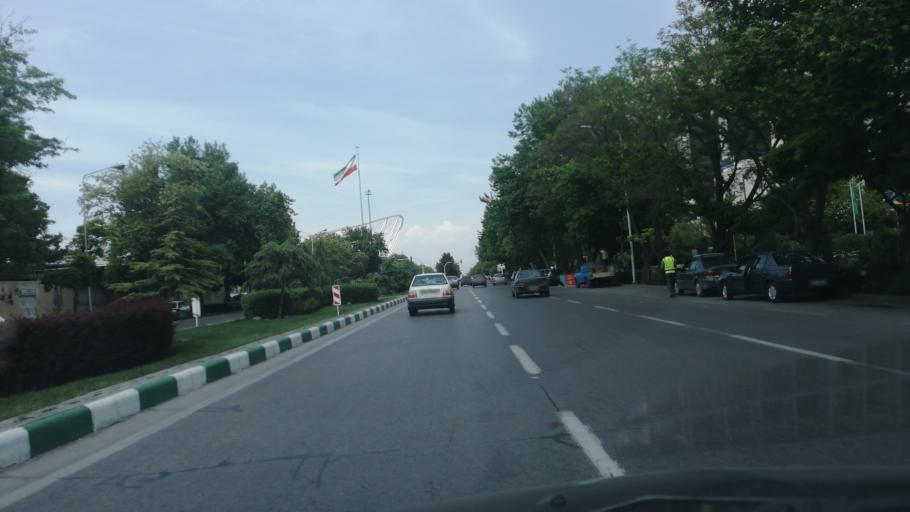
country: IR
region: Razavi Khorasan
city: Mashhad
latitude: 36.3228
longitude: 59.5687
